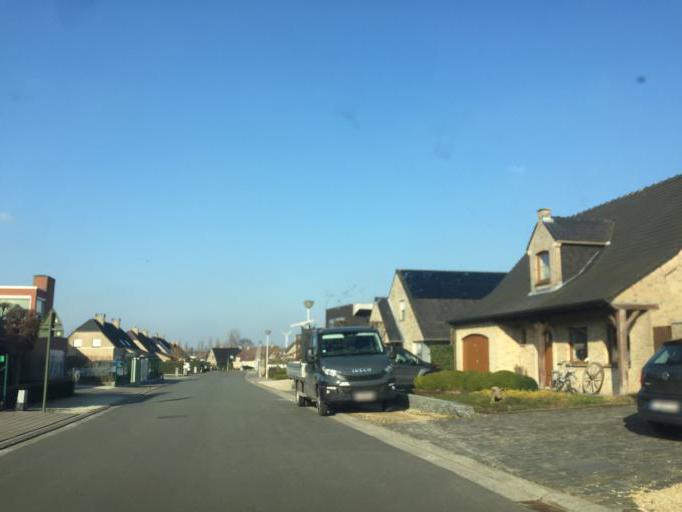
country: BE
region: Flanders
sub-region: Provincie West-Vlaanderen
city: Roeselare
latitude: 50.9181
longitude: 3.1568
